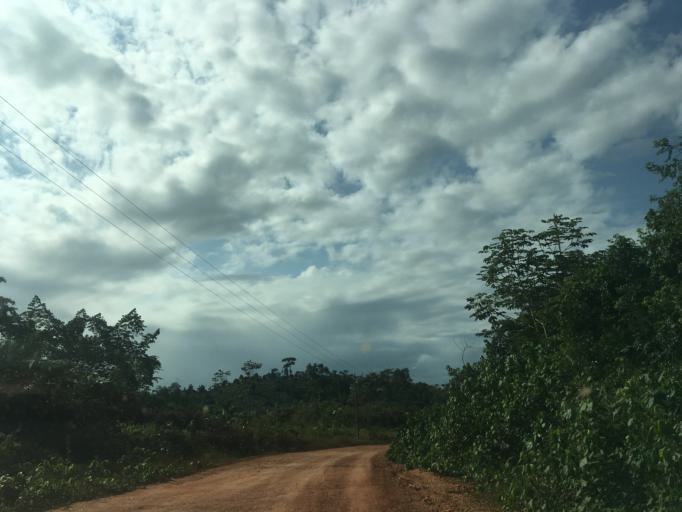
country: GH
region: Western
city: Wassa-Akropong
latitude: 5.9151
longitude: -2.4057
